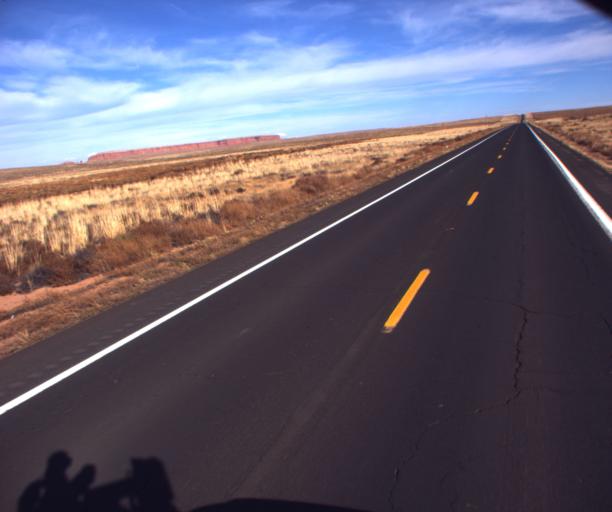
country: US
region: Arizona
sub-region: Apache County
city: Lukachukai
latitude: 36.9624
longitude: -109.4290
